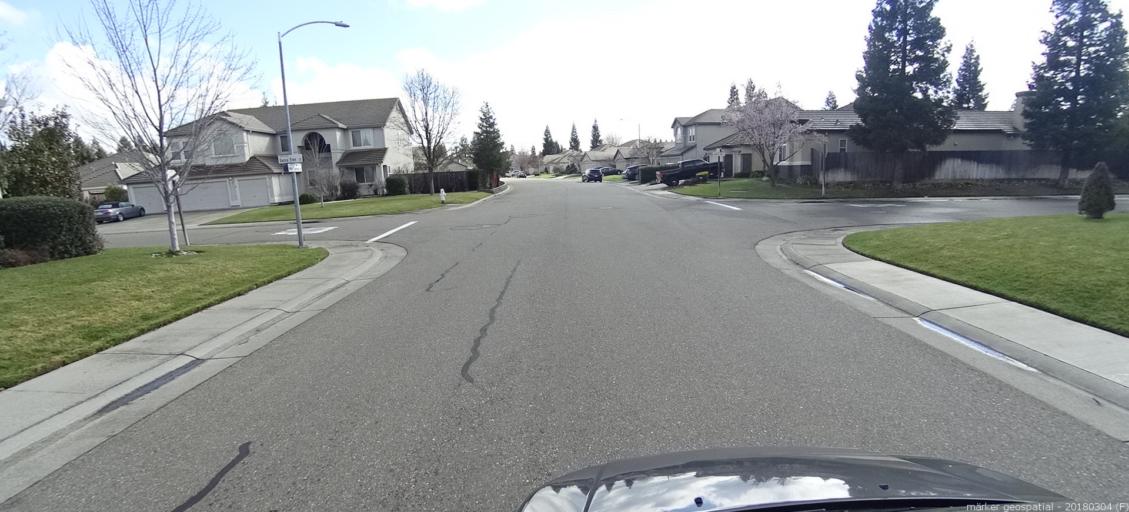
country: US
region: California
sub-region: Sacramento County
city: Vineyard
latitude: 38.4605
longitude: -121.3222
